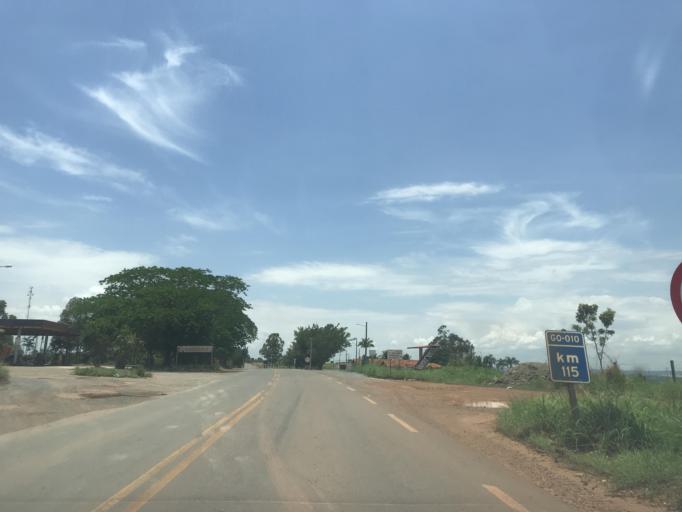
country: BR
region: Goias
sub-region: Vianopolis
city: Vianopolis
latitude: -16.5857
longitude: -48.3457
